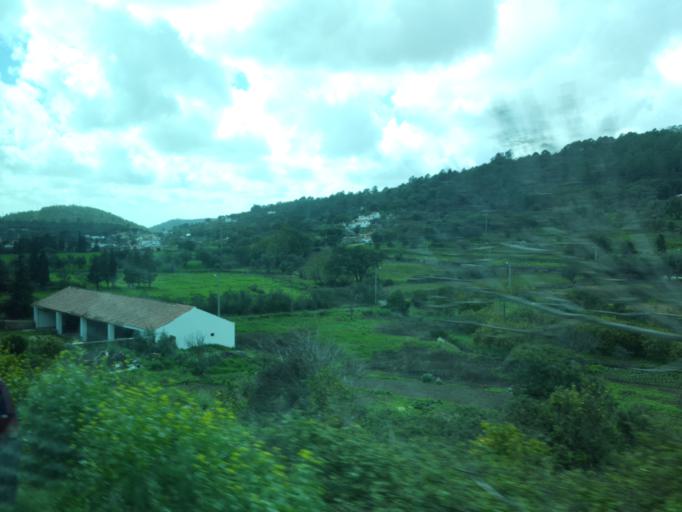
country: PT
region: Faro
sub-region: Monchique
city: Monchique
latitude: 37.3021
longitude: -8.5629
